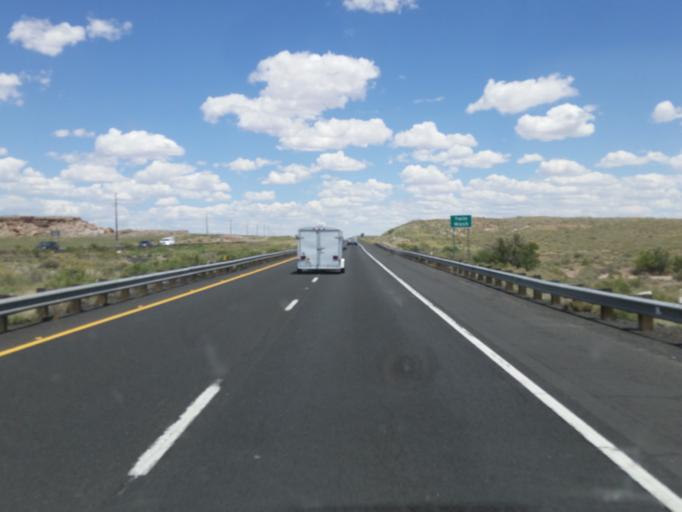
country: US
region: Arizona
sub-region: Navajo County
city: Holbrook
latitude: 34.9910
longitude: -109.9841
